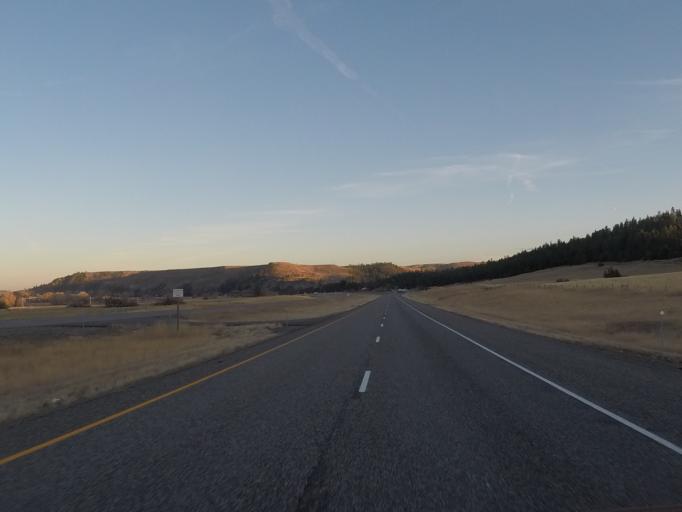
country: US
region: Montana
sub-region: Sweet Grass County
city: Big Timber
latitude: 45.7401
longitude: -109.7646
